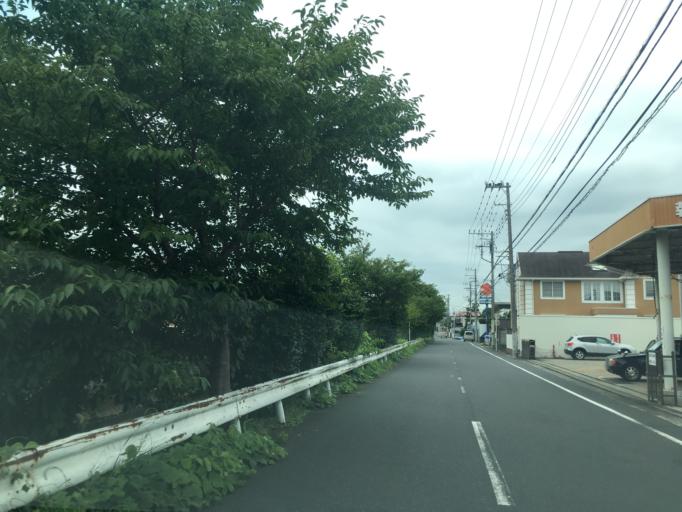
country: JP
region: Kanagawa
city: Odawara
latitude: 35.2581
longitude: 139.1688
